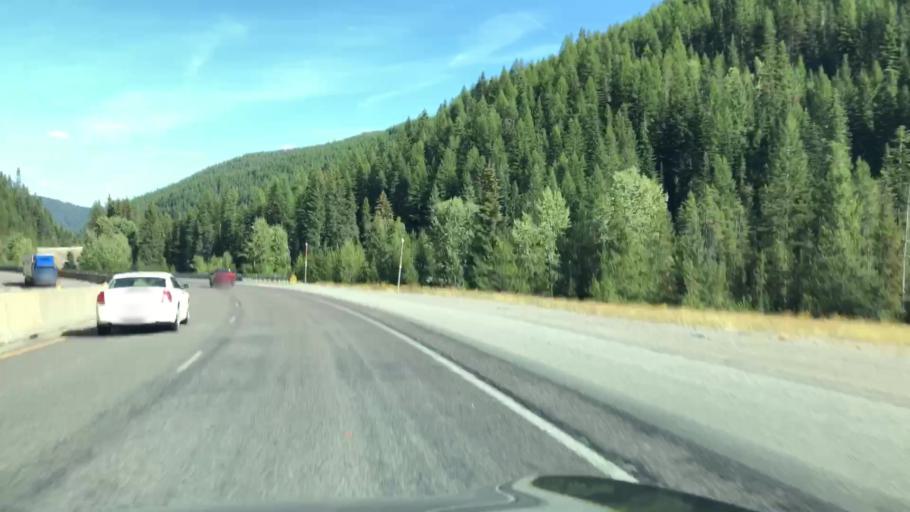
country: US
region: Montana
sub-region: Sanders County
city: Thompson Falls
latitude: 47.4158
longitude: -115.5868
